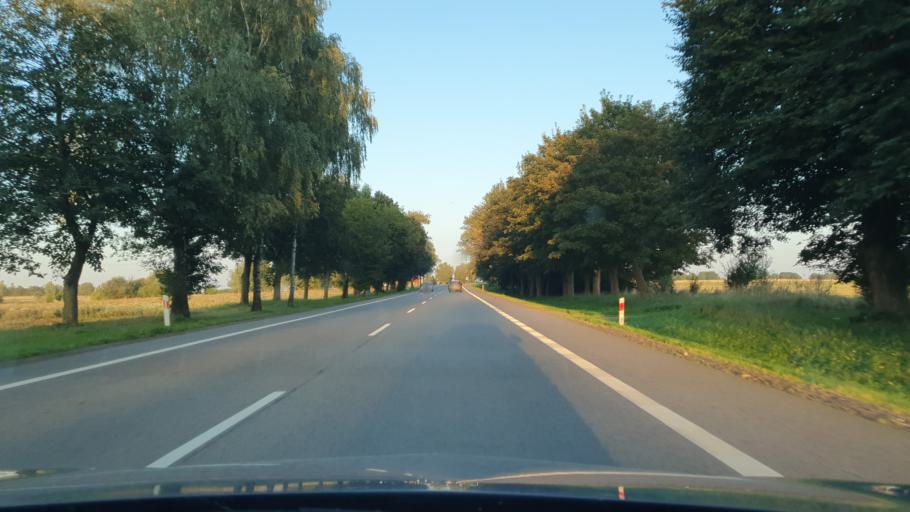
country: PL
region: Pomeranian Voivodeship
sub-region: Powiat slupski
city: Potegowo
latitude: 54.4772
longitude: 17.5113
